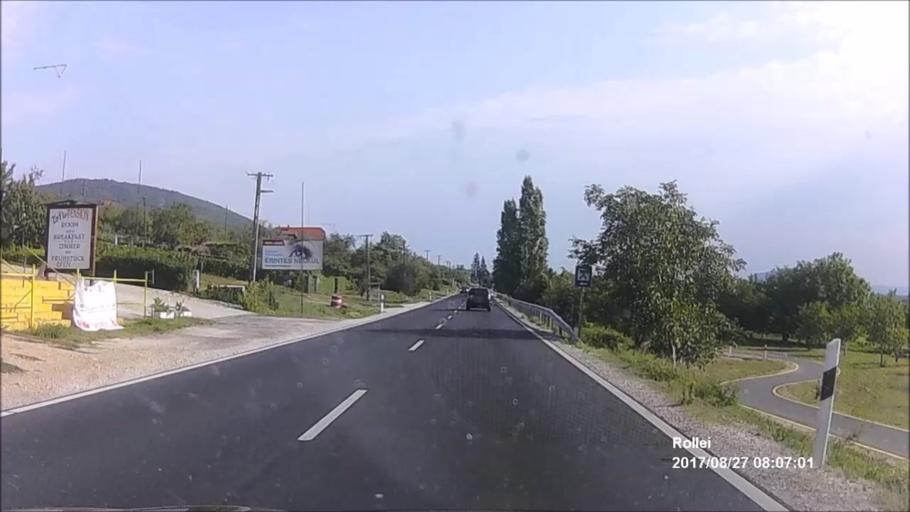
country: HU
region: Zala
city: Vonyarcvashegy
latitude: 46.7748
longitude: 17.3646
